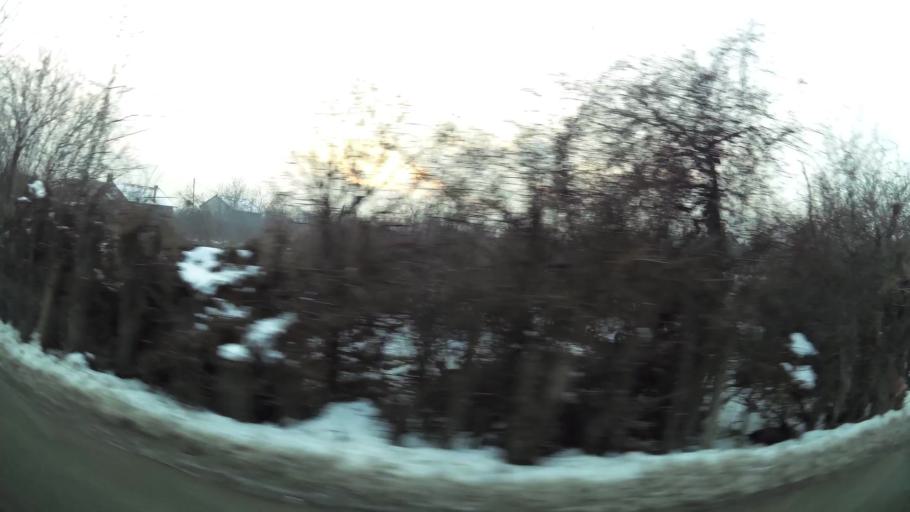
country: MK
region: Suto Orizari
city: Suto Orizare
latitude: 42.0294
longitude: 21.4191
